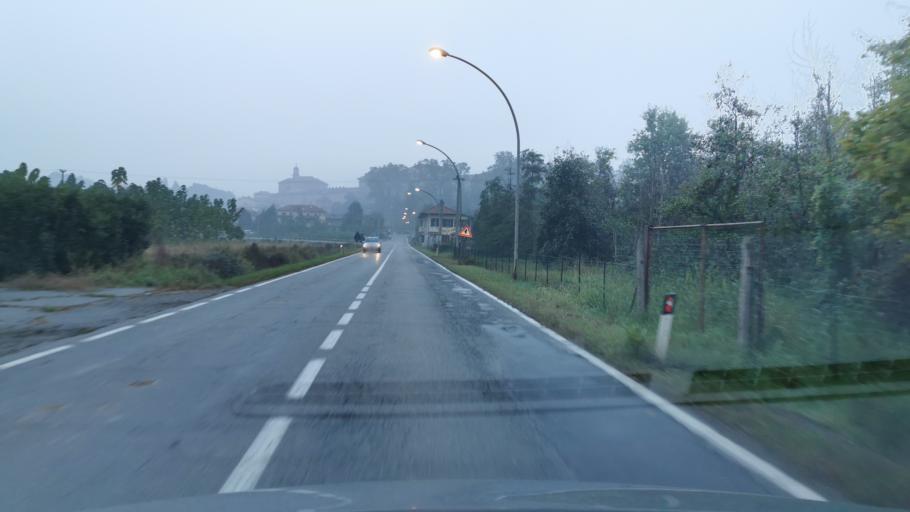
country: IT
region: Piedmont
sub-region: Provincia di Torino
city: Aglie
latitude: 45.3568
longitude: 7.7682
